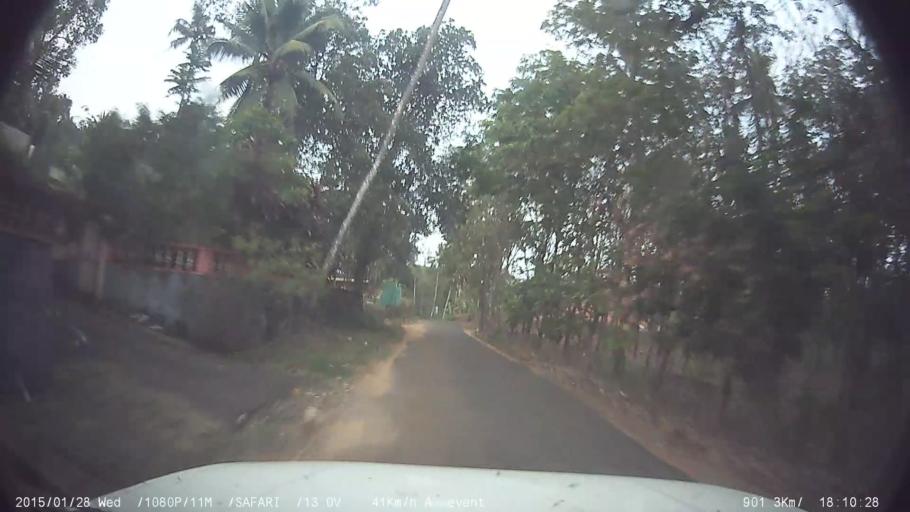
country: IN
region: Kerala
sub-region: Kottayam
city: Palackattumala
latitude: 9.7460
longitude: 76.5703
